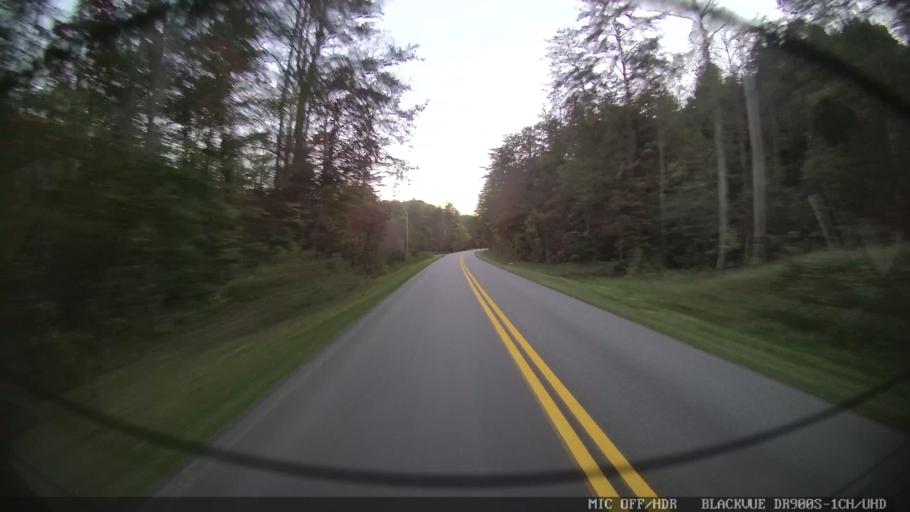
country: US
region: Georgia
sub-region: Union County
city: Blairsville
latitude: 34.8753
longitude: -83.8793
